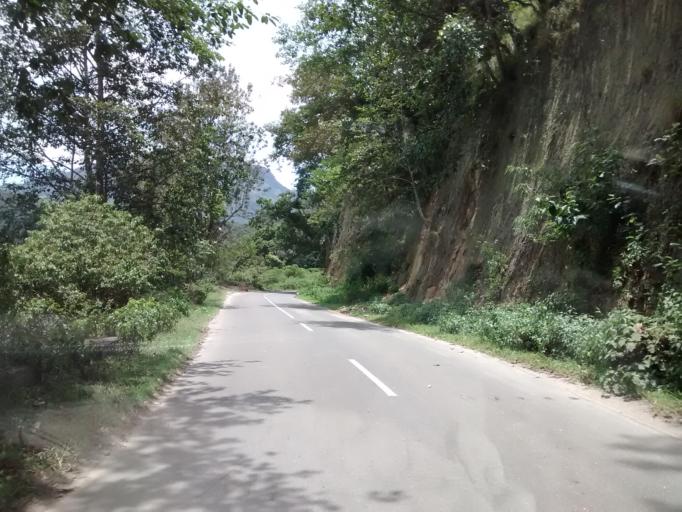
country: IN
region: Kerala
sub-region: Idukki
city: Munnar
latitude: 10.1416
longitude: 77.2025
